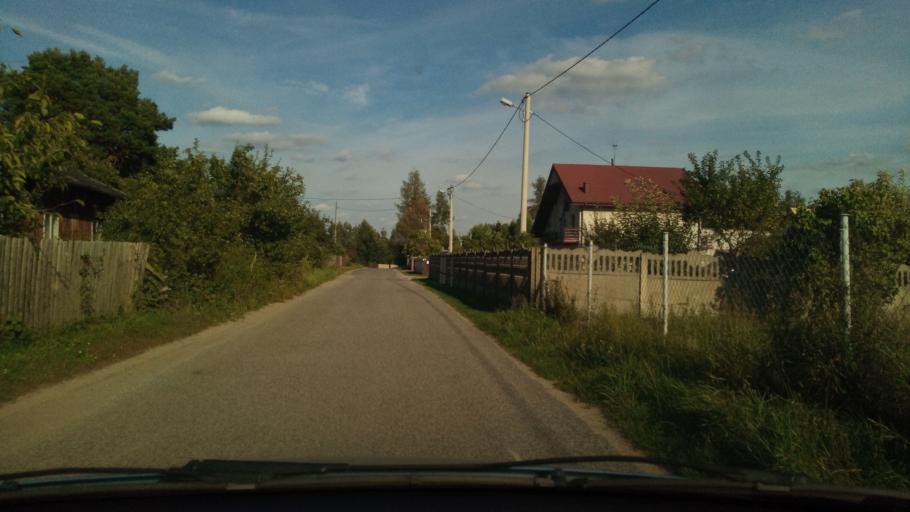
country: PL
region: Lodz Voivodeship
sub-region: Powiat piotrkowski
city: Sulejow
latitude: 51.4092
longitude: 19.8758
